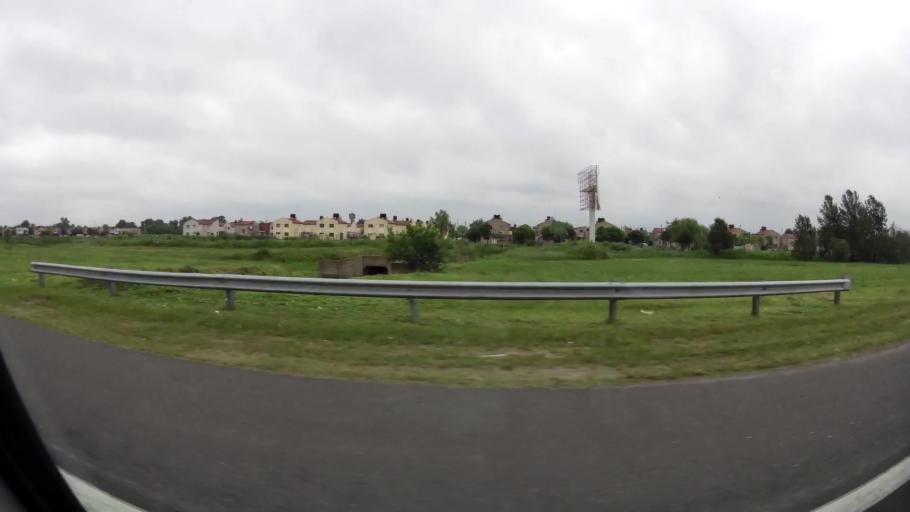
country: AR
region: Buenos Aires
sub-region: Partido de La Plata
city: La Plata
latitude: -34.8759
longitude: -57.9707
